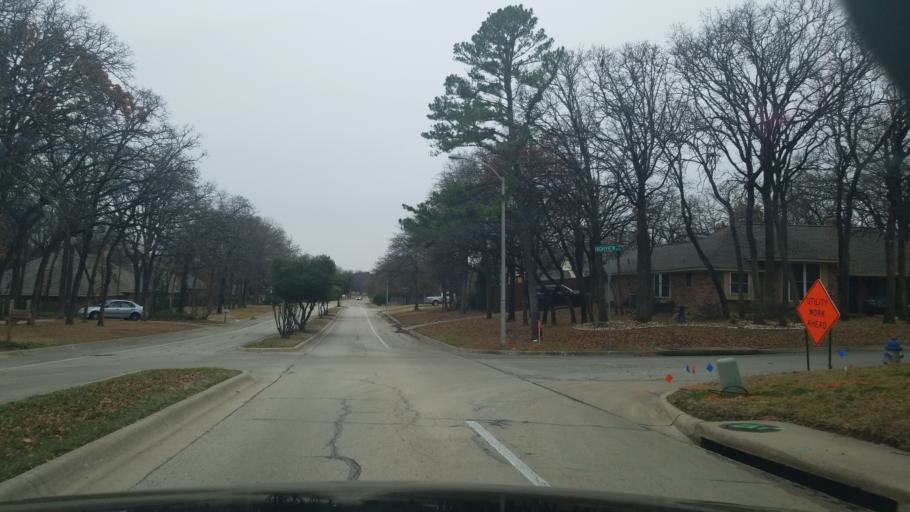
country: US
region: Texas
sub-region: Denton County
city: Denton
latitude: 33.1736
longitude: -97.1296
